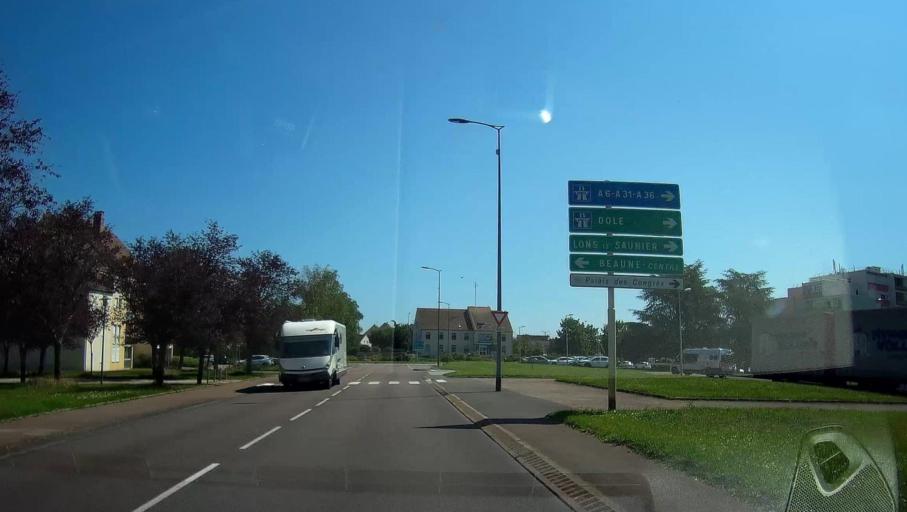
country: FR
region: Bourgogne
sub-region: Departement de la Cote-d'Or
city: Beaune
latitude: 47.0181
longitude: 4.8341
